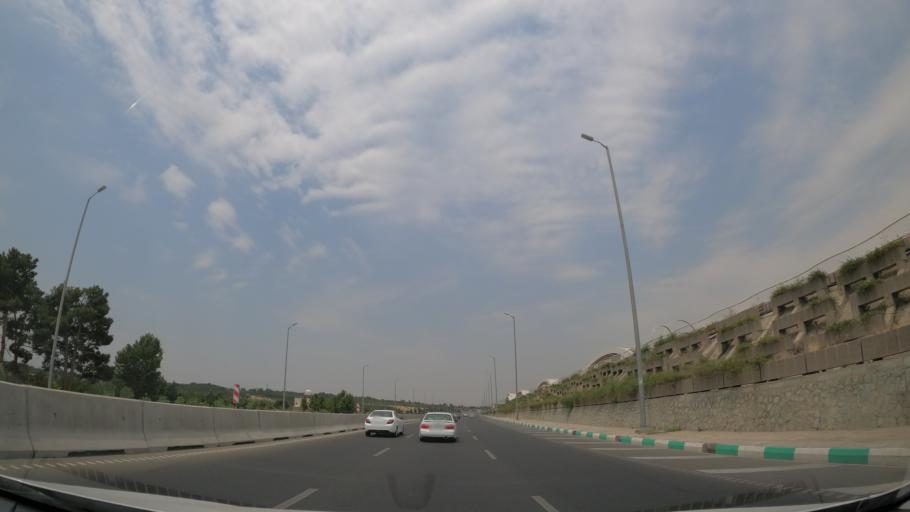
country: IR
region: Tehran
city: Shahr-e Qods
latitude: 35.7390
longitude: 51.2185
